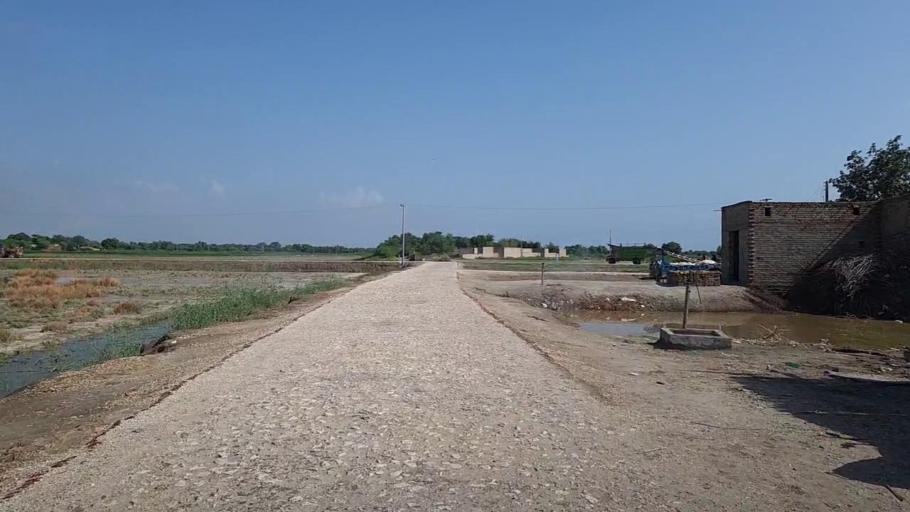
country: PK
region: Sindh
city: Bhiria
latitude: 26.8698
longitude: 68.2339
